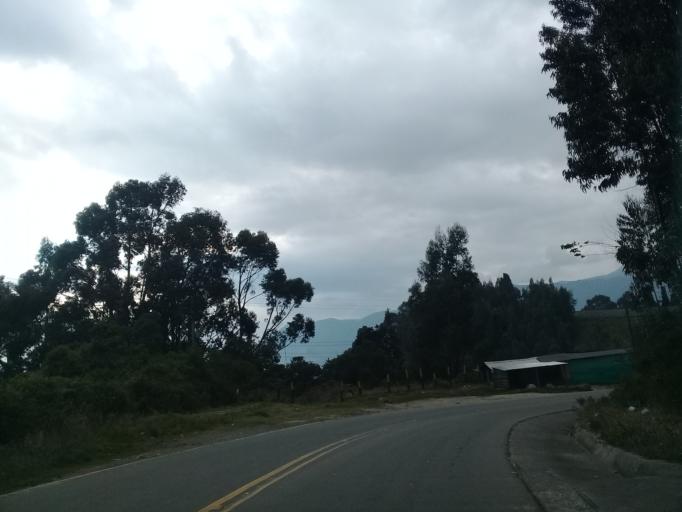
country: CO
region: Cundinamarca
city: Zipaquira
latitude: 5.0304
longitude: -74.0340
